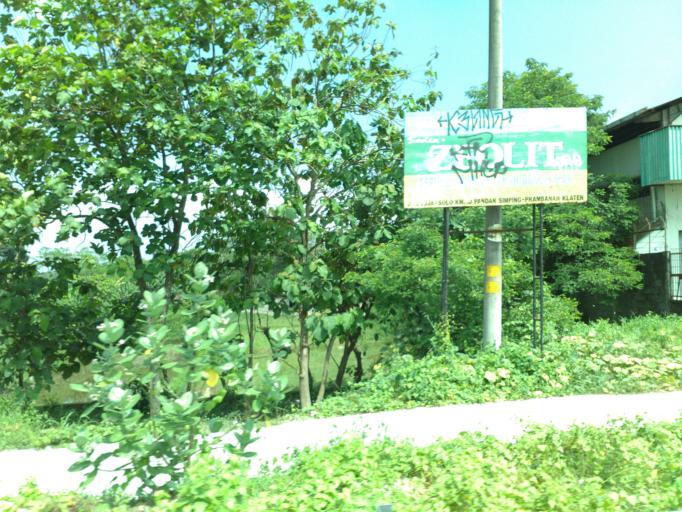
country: ID
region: Central Java
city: Candi Prambanan
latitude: -7.7421
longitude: 110.5310
